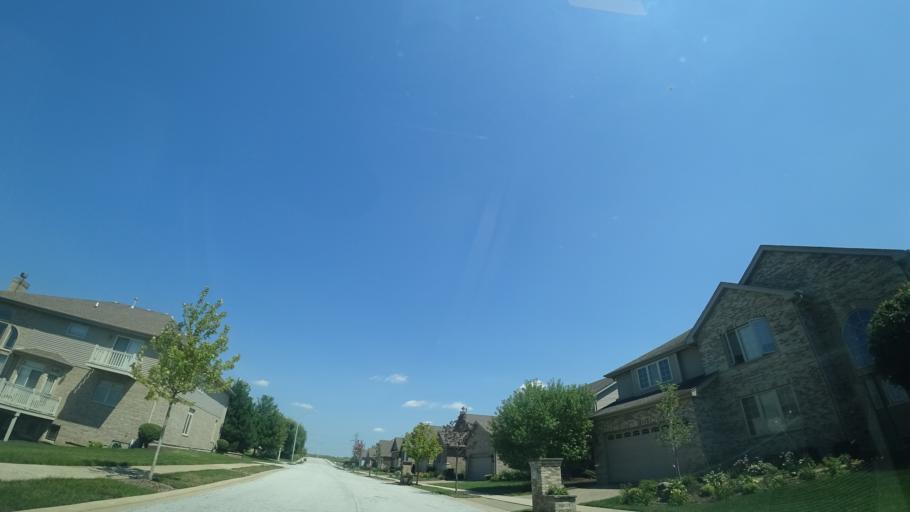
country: US
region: Illinois
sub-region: Will County
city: Mokena
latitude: 41.5591
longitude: -87.8871
